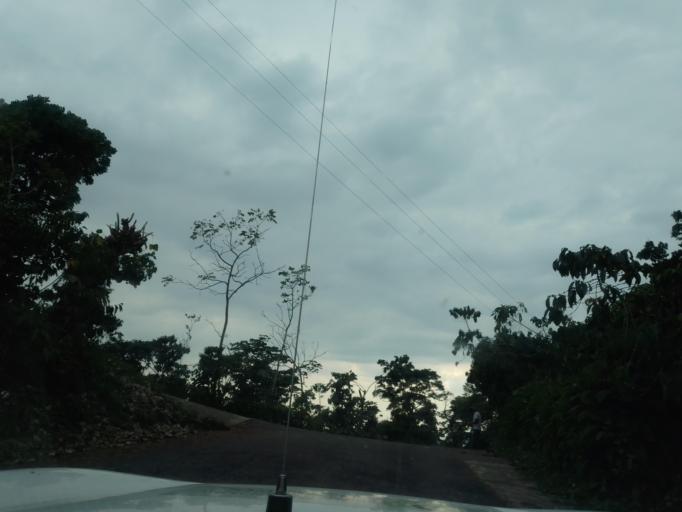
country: MX
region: Chiapas
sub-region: Union Juarez
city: Santo Domingo
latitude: 15.0489
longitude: -92.1197
